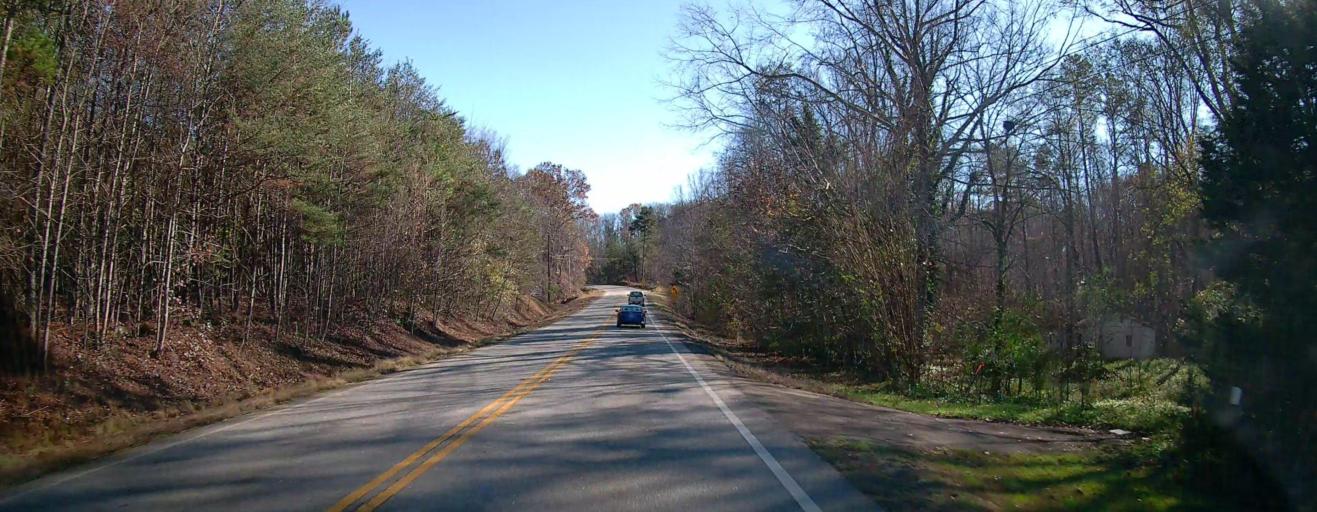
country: US
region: Georgia
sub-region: Hall County
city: Lula
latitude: 34.4088
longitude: -83.7100
